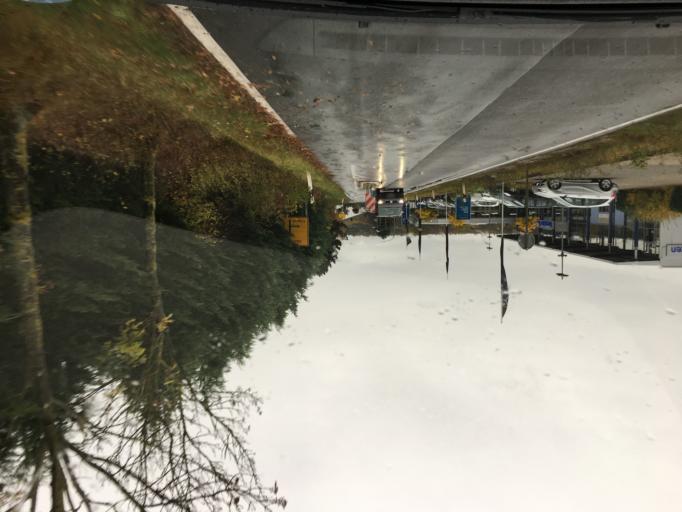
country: DE
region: North Rhine-Westphalia
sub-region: Regierungsbezirk Koln
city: Vettweiss
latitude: 50.6872
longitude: 6.5765
